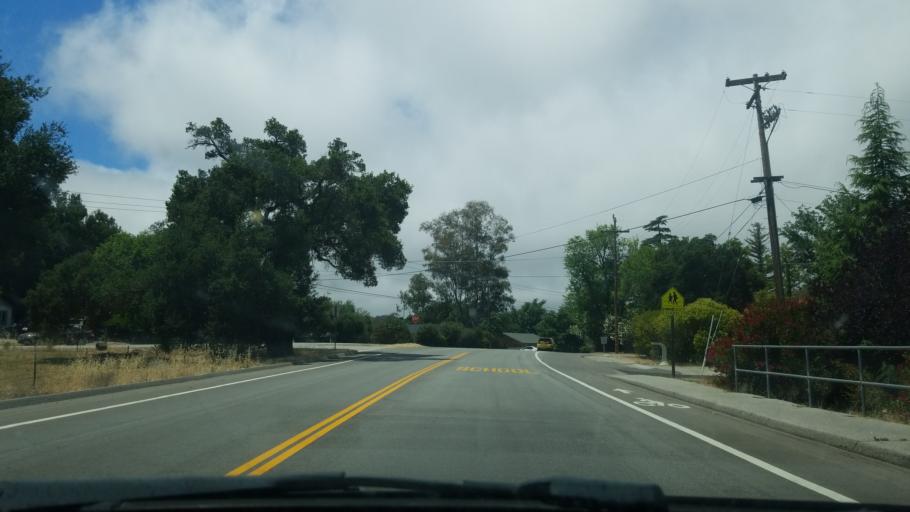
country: US
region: California
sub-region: San Luis Obispo County
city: Atascadero
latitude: 35.4648
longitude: -120.6533
